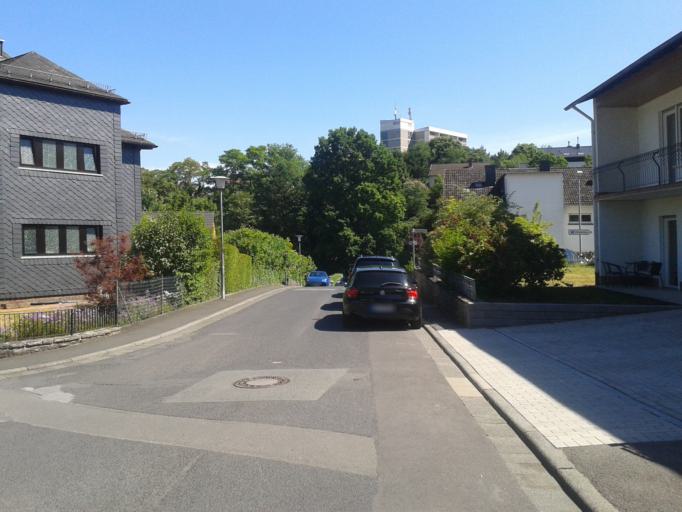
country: DE
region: Hesse
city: Herborn
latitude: 50.6837
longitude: 8.2937
